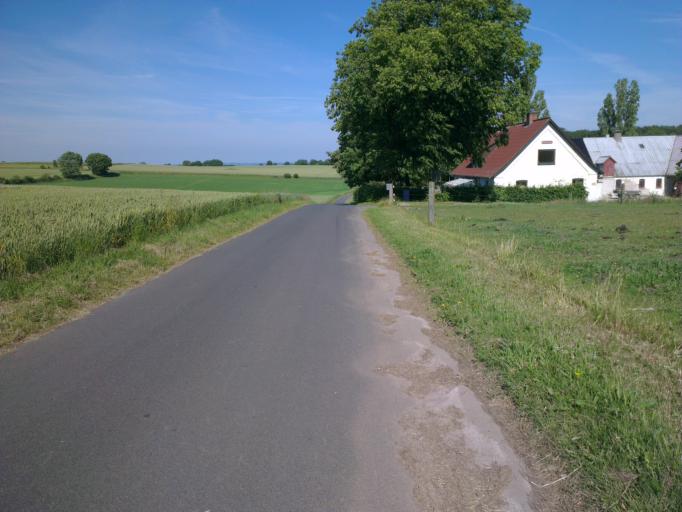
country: DK
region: Capital Region
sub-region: Frederikssund Kommune
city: Skibby
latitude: 55.7847
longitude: 11.8805
